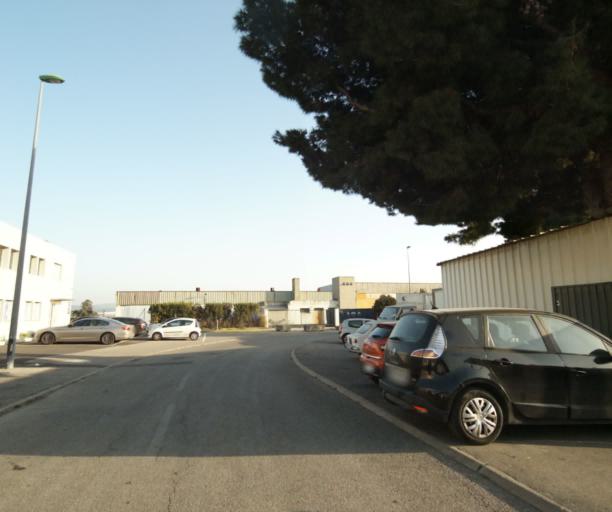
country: FR
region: Provence-Alpes-Cote d'Azur
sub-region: Departement des Bouches-du-Rhone
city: Saint-Victoret
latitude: 43.4314
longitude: 5.2382
